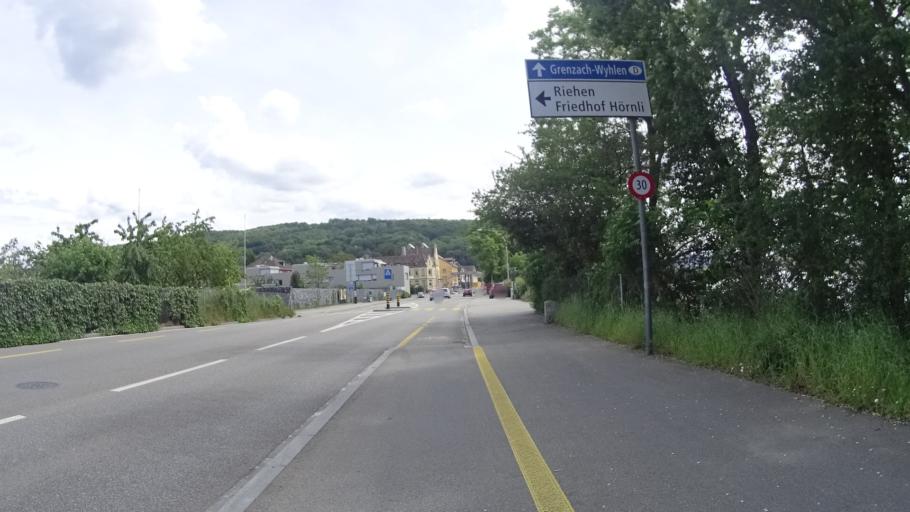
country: CH
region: Basel-Landschaft
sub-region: Bezirk Arlesheim
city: Birsfelden
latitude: 47.5626
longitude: 7.6329
